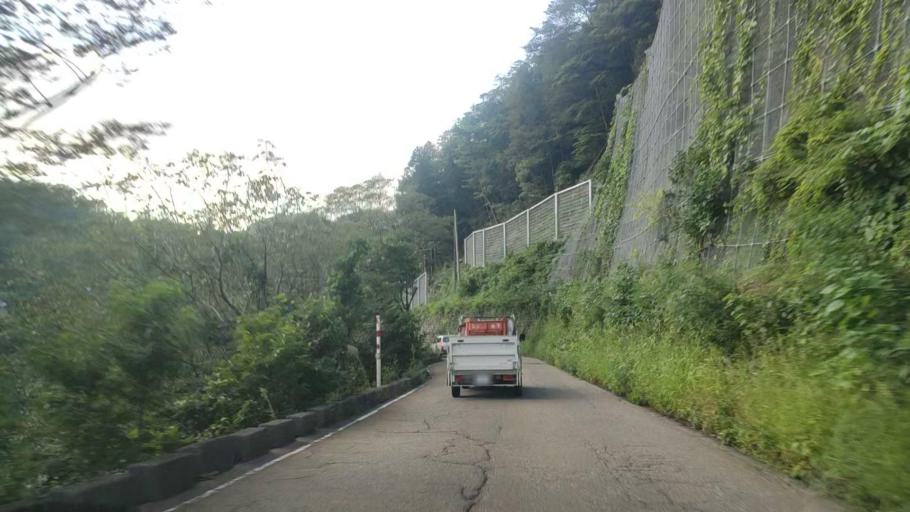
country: JP
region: Toyama
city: Nanto-shi
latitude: 36.5580
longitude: 137.0090
